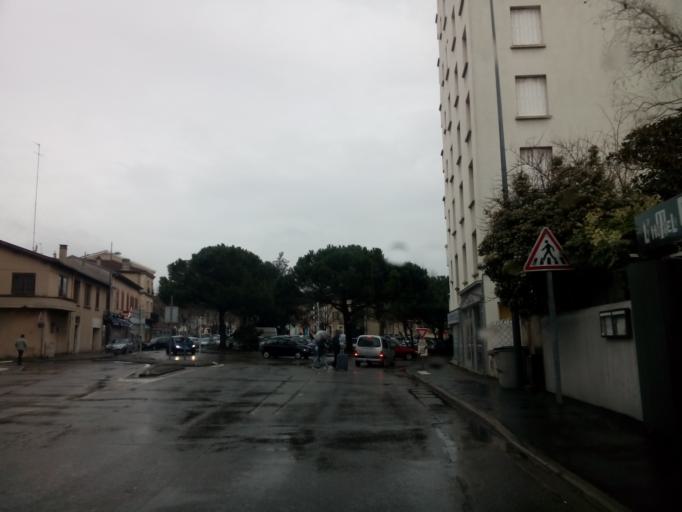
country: FR
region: Rhone-Alpes
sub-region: Departement de la Drome
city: Romans-sur-Isere
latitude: 45.0459
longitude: 5.0456
